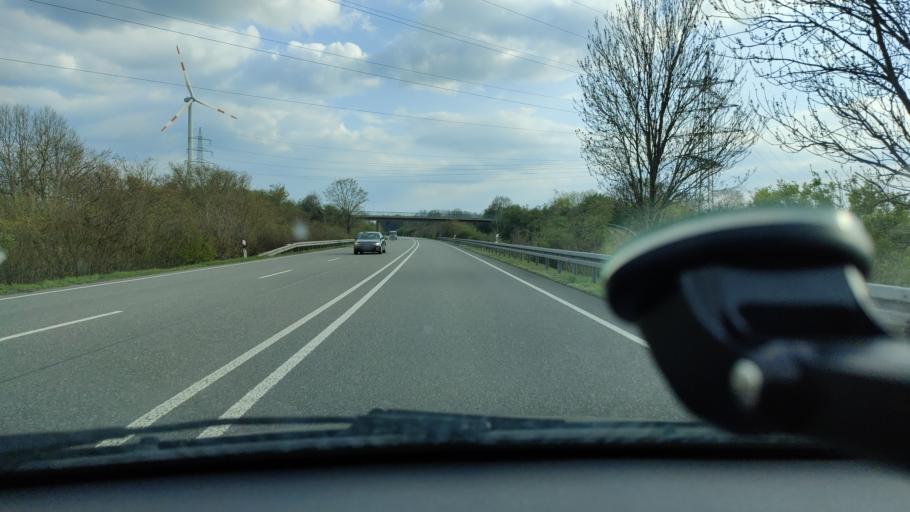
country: DE
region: North Rhine-Westphalia
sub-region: Regierungsbezirk Dusseldorf
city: Bocholt
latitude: 51.7931
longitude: 6.5773
